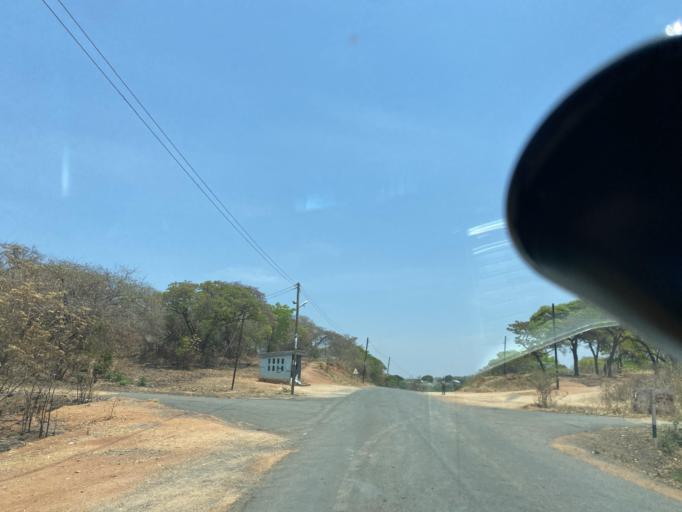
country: ZM
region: Lusaka
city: Kafue
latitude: -15.8671
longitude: 28.4391
